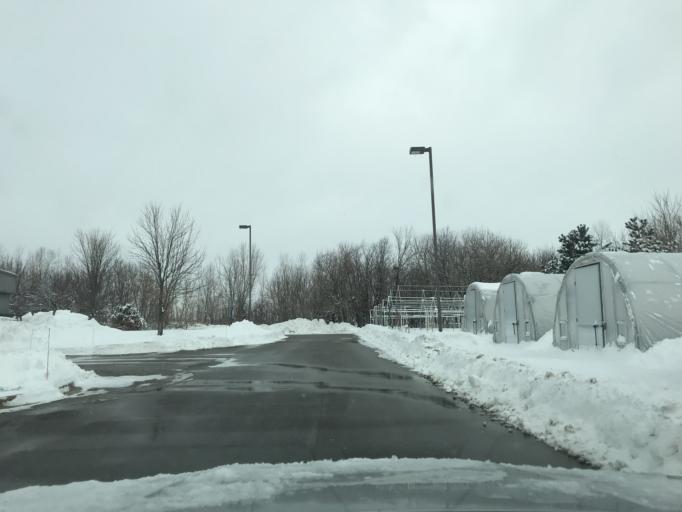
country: US
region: Wisconsin
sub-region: Dane County
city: Sun Prairie
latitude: 43.1606
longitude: -89.2815
